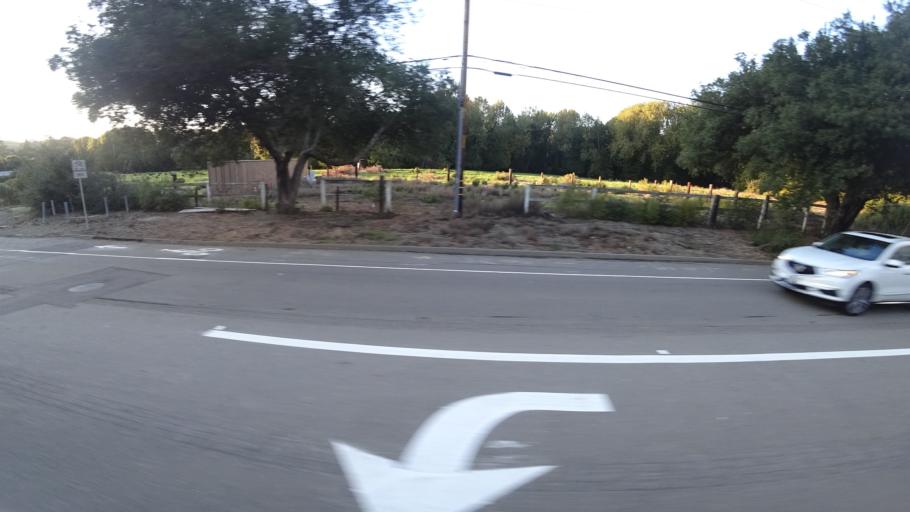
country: US
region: California
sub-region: Alameda County
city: Dublin
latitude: 37.6954
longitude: -121.9449
